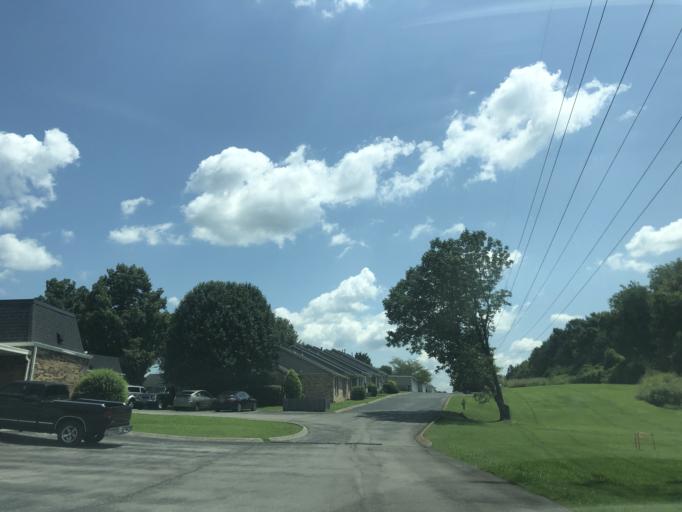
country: US
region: Tennessee
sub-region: Wilson County
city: Green Hill
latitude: 36.1598
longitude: -86.5897
